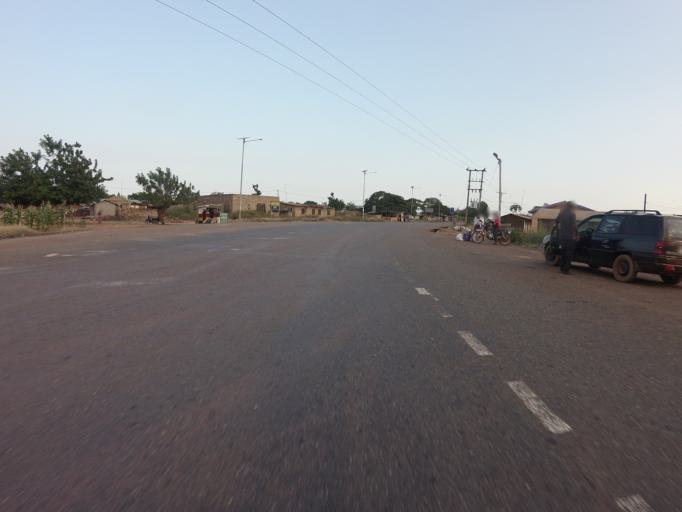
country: GH
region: Volta
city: Anloga
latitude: 6.0748
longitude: 0.6043
